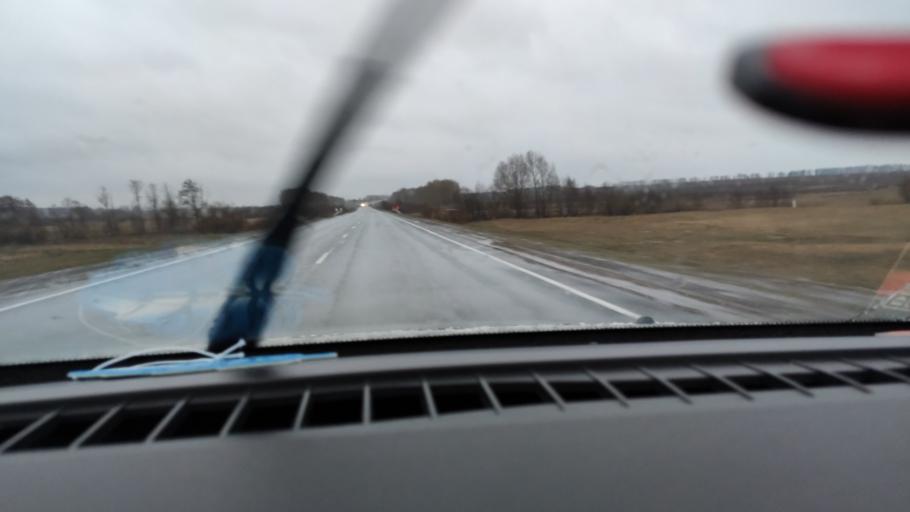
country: RU
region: Tatarstan
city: Mendeleyevsk
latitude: 55.9676
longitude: 52.3168
